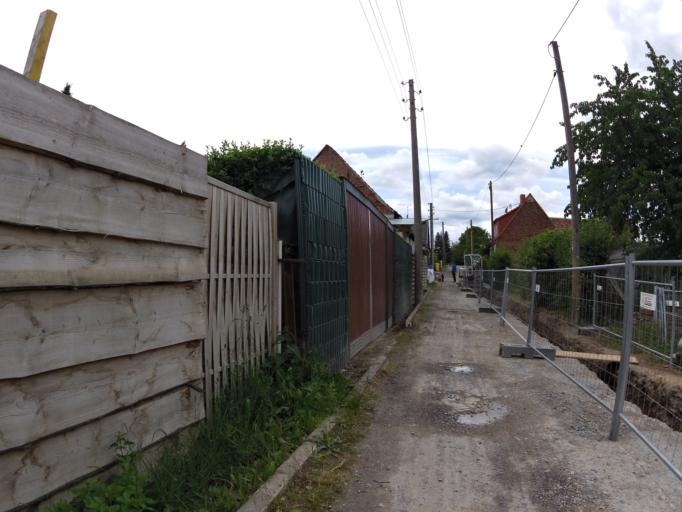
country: DE
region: Thuringia
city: Oberdorla
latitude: 51.1688
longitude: 10.4256
